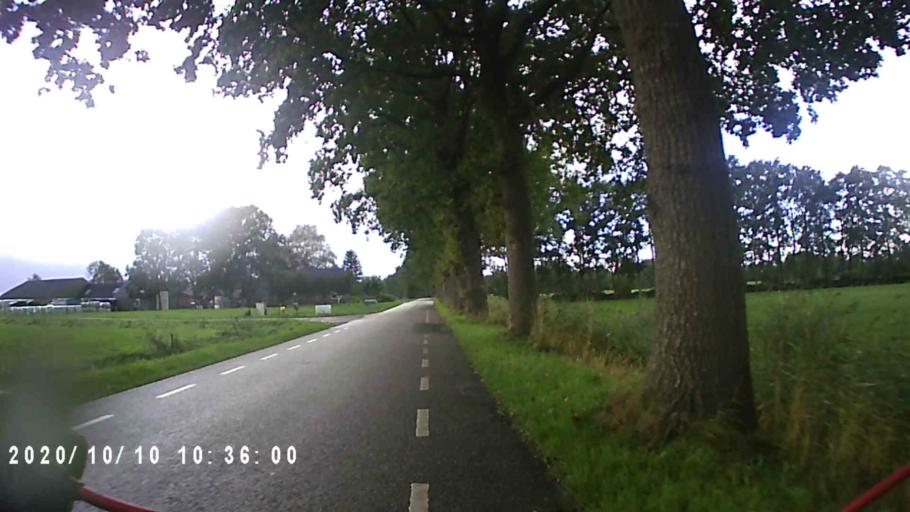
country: NL
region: Groningen
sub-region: Gemeente Grootegast
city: Grootegast
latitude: 53.1881
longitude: 6.3061
